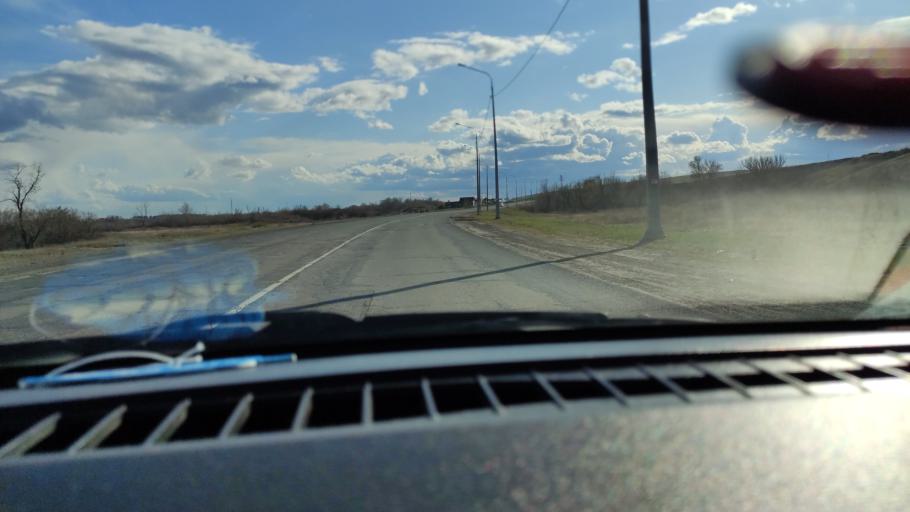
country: RU
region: Saratov
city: Sinodskoye
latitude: 52.0878
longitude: 46.8049
